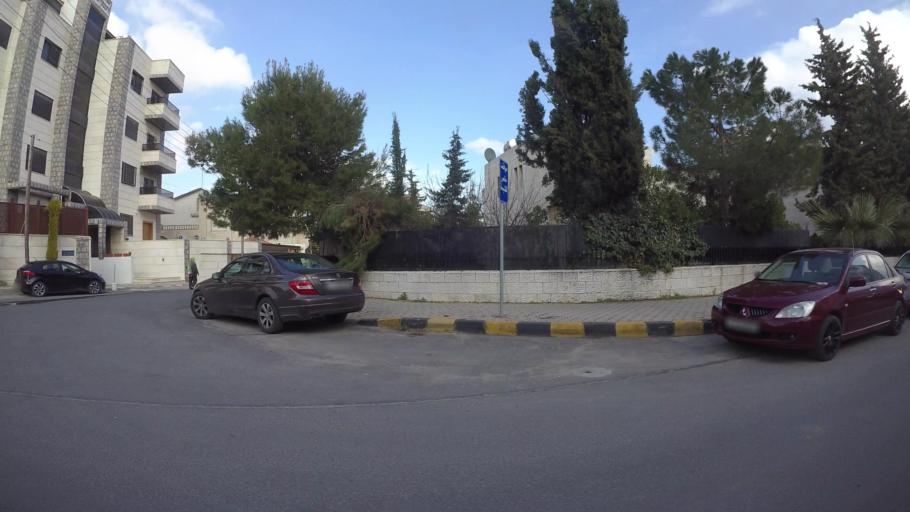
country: JO
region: Amman
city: Wadi as Sir
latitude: 31.9801
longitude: 35.8501
